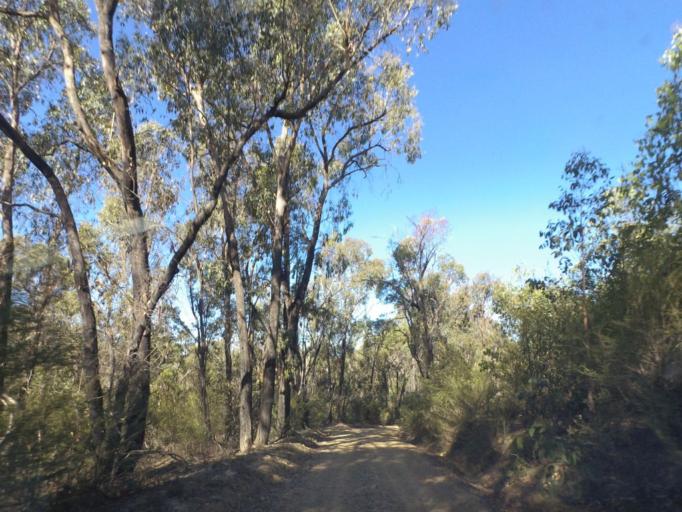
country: AU
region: Victoria
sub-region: Murrindindi
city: Kinglake West
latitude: -37.4624
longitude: 145.3768
